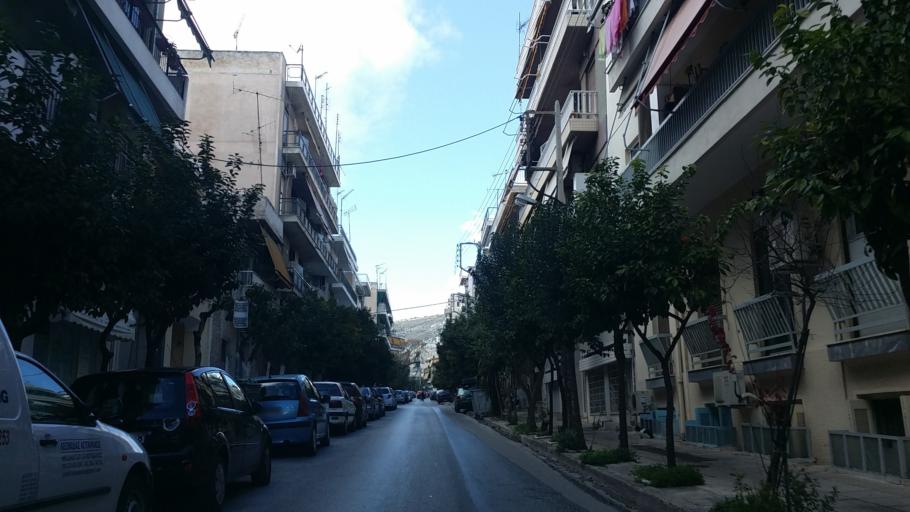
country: GR
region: Attica
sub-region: Nomos Piraios
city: Korydallos
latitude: 37.9781
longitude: 23.6451
